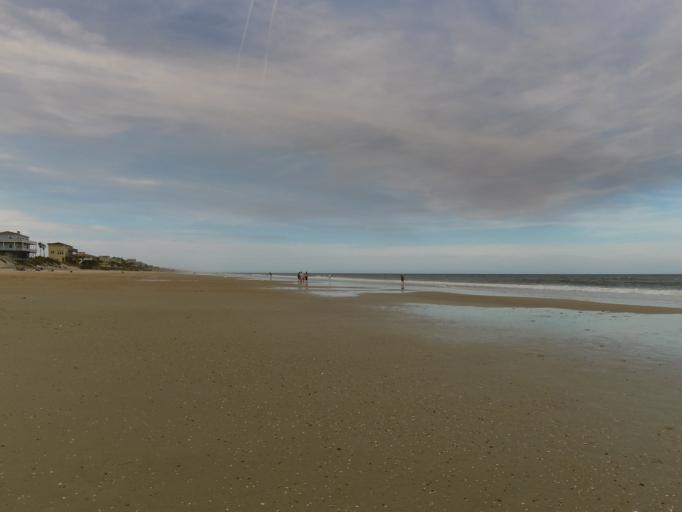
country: US
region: Florida
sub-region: Saint Johns County
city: Villano Beach
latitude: 29.9403
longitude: -81.2997
